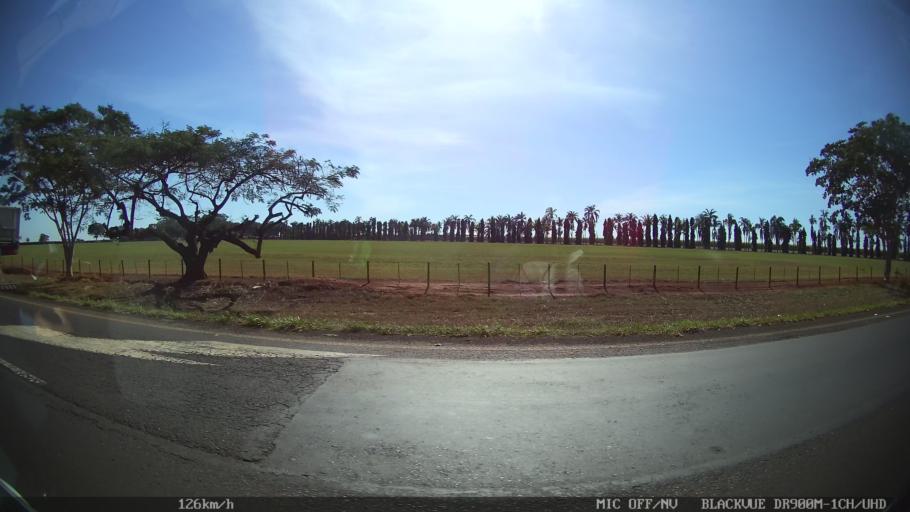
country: BR
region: Sao Paulo
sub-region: Barretos
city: Barretos
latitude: -20.5677
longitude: -48.6655
